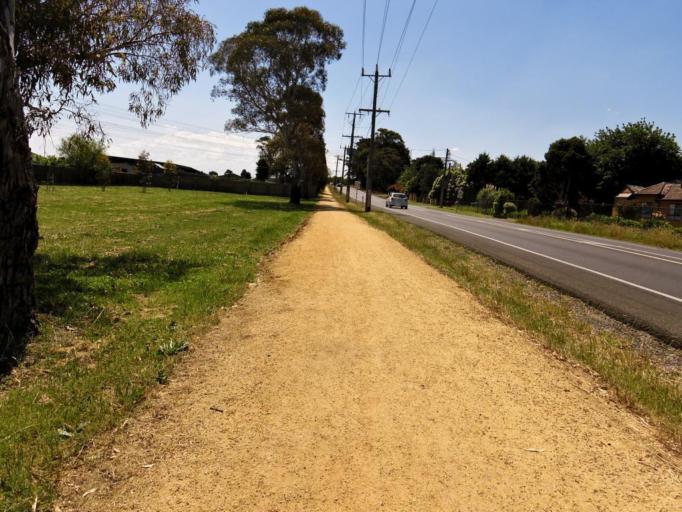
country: AU
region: Victoria
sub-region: Casey
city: Narre Warren South
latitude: -38.0373
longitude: 145.2876
